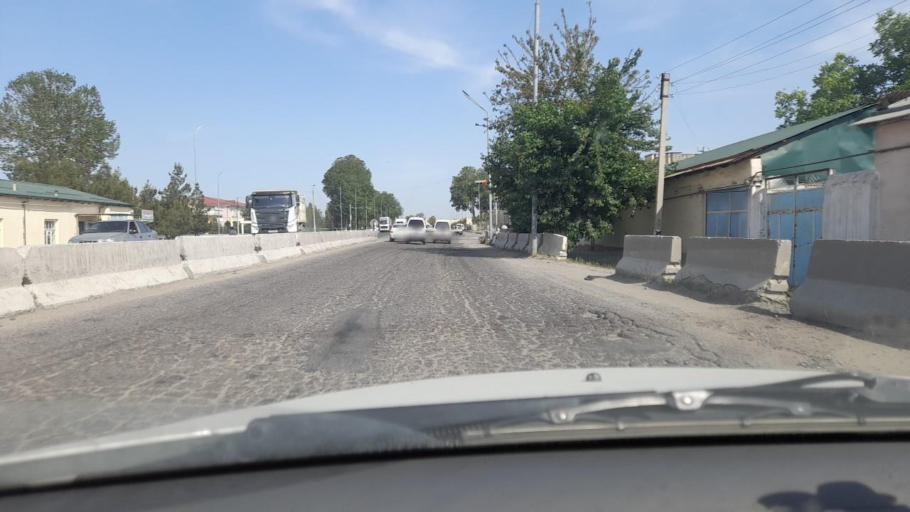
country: UZ
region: Samarqand
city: Daxbet
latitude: 39.7629
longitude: 66.9117
